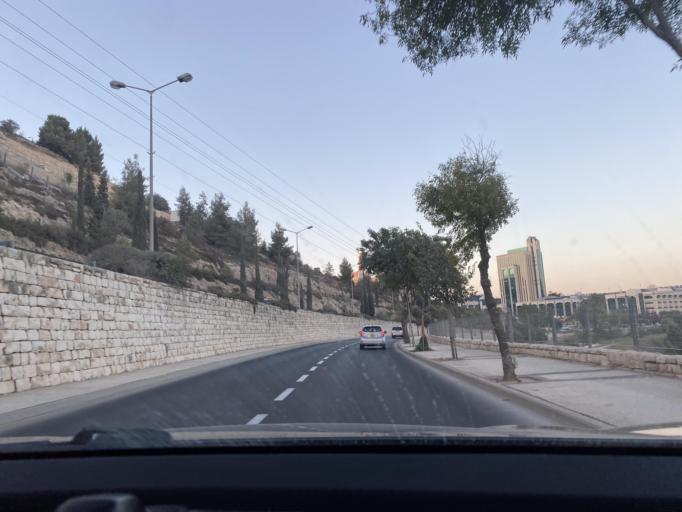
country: PS
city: Khallat Hamamah
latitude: 31.7471
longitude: 35.1817
